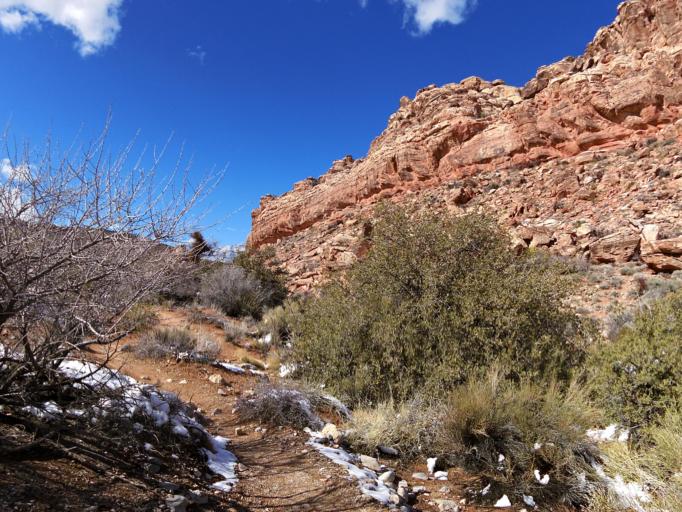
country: US
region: Nevada
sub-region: Clark County
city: Summerlin South
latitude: 36.1413
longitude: -115.4217
